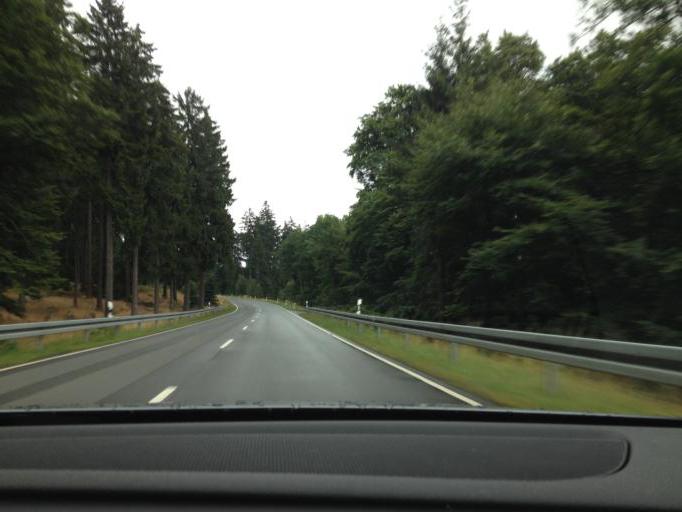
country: DE
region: Hesse
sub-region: Regierungsbezirk Darmstadt
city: Schlangenbad
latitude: 50.1076
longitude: 8.1277
